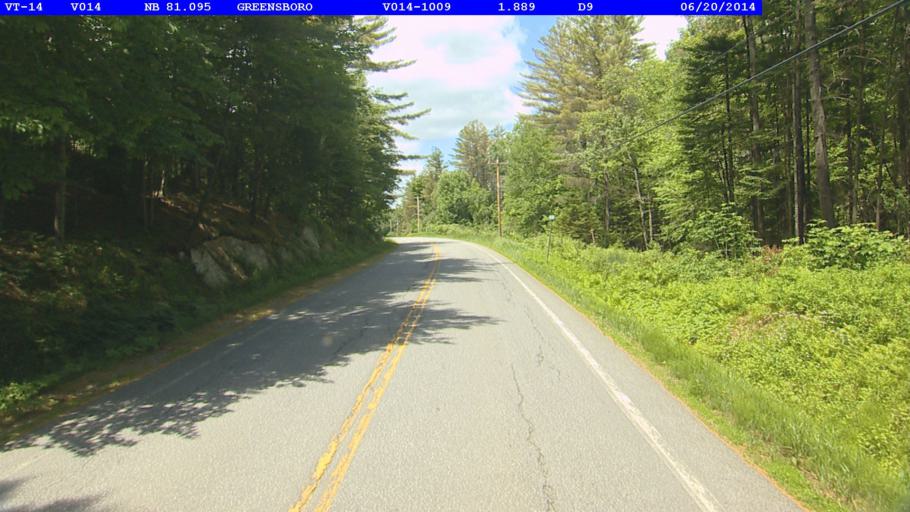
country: US
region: Vermont
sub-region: Caledonia County
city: Hardwick
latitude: 44.6060
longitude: -72.3585
